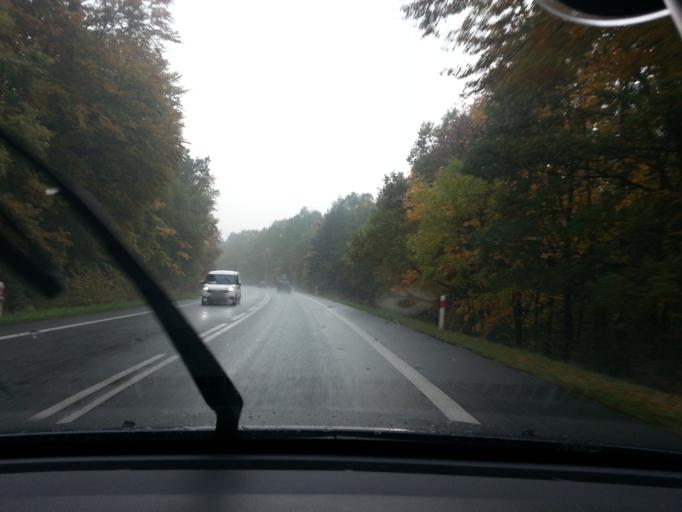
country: PL
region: Silesian Voivodeship
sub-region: Powiat gliwicki
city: Pilchowice
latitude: 50.1765
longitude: 18.5454
